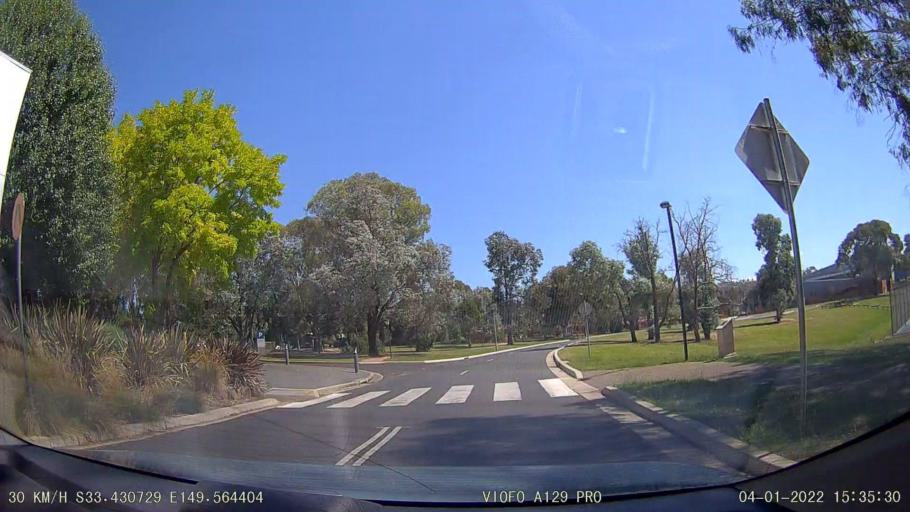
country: AU
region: New South Wales
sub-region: Bathurst Regional
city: Bathurst
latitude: -33.4307
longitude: 149.5644
